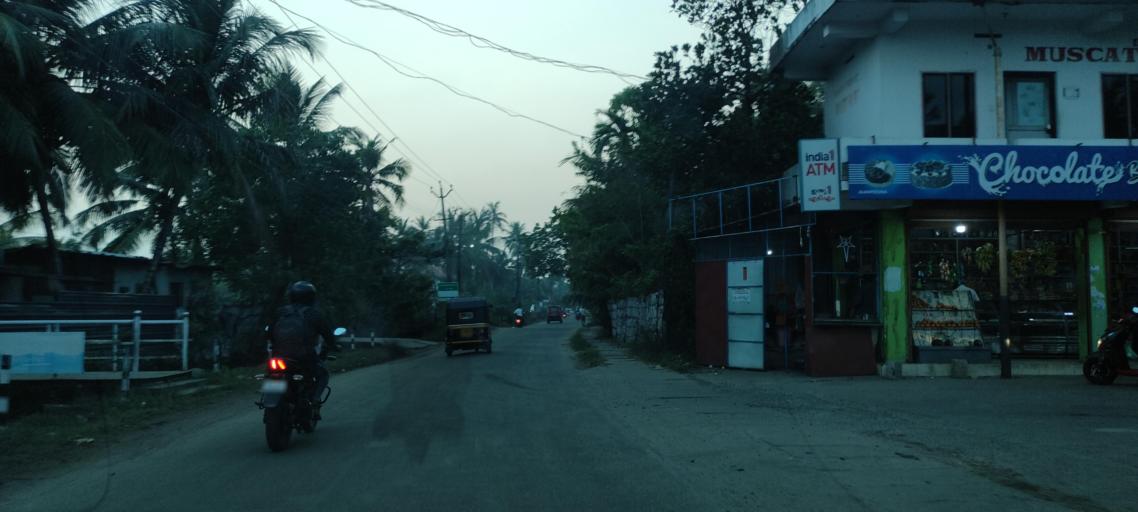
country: IN
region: Kerala
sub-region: Alappuzha
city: Kayankulam
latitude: 9.1184
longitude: 76.4857
